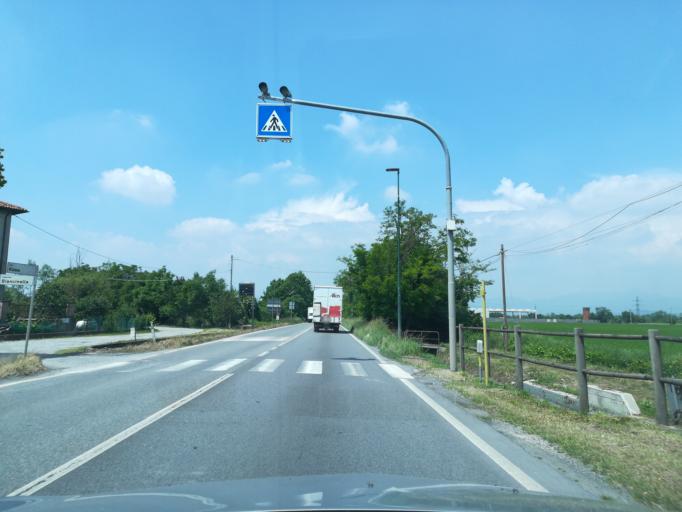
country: IT
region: Lombardy
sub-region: Provincia di Bergamo
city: Cavernago
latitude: 45.6352
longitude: 9.7597
